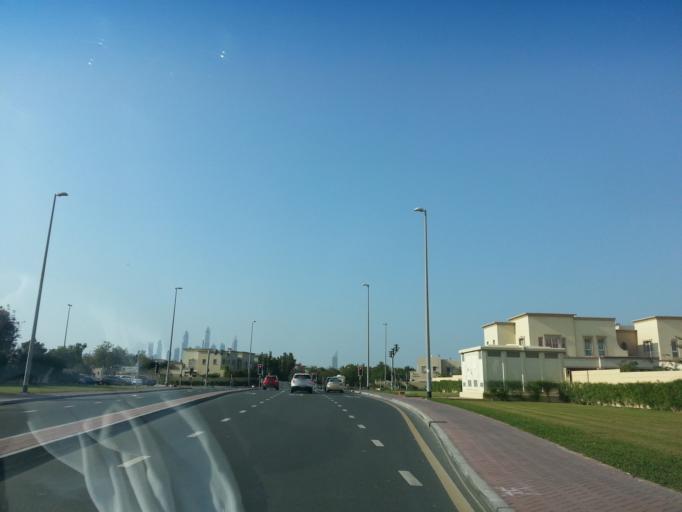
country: AE
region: Dubai
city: Dubai
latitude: 25.0577
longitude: 55.1793
